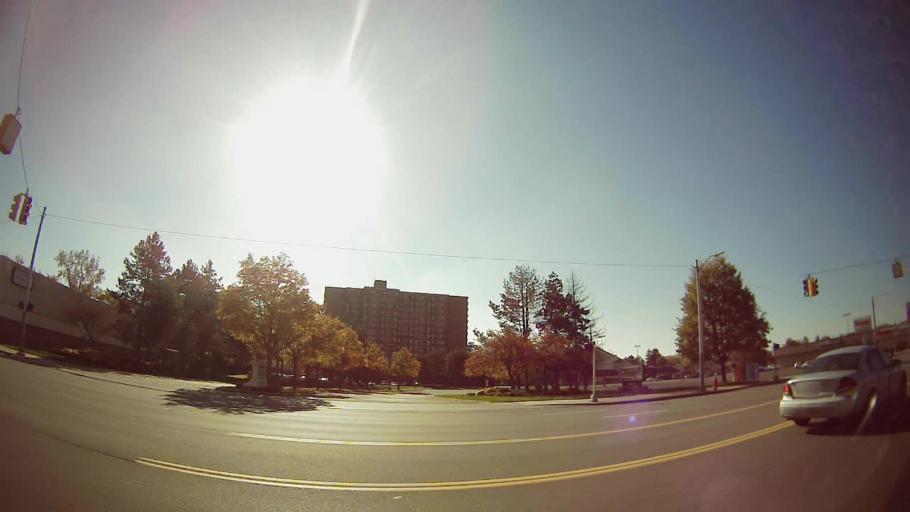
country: US
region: Michigan
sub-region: Wayne County
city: Dearborn Heights
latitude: 42.3719
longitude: -83.2384
